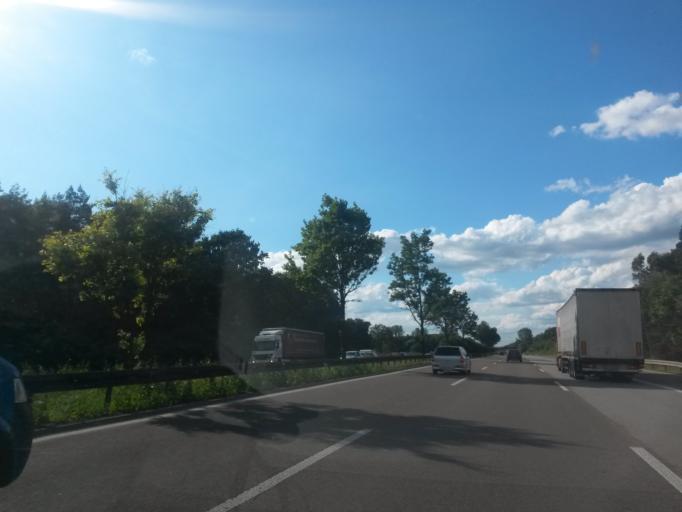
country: DE
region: Bavaria
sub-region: Upper Bavaria
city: Manching
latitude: 48.6787
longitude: 11.5027
